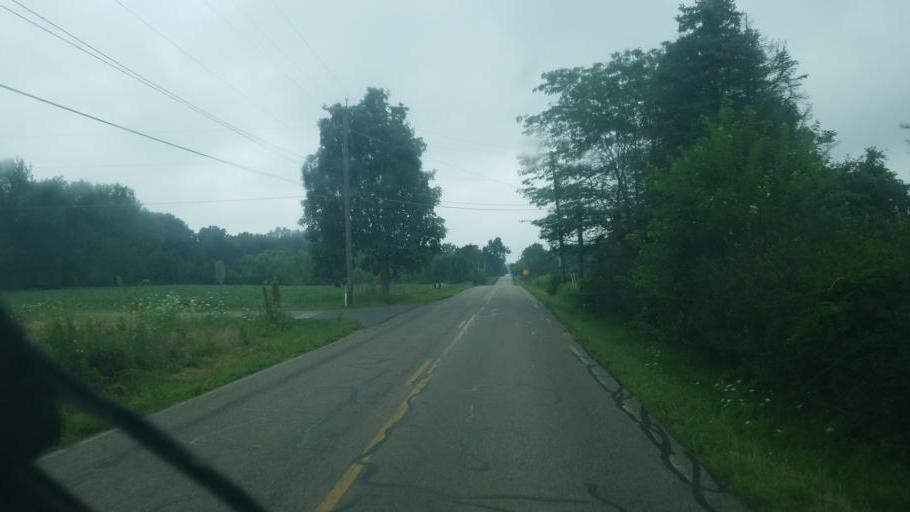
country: US
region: Ohio
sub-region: Delaware County
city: Sunbury
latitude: 40.2539
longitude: -82.9381
